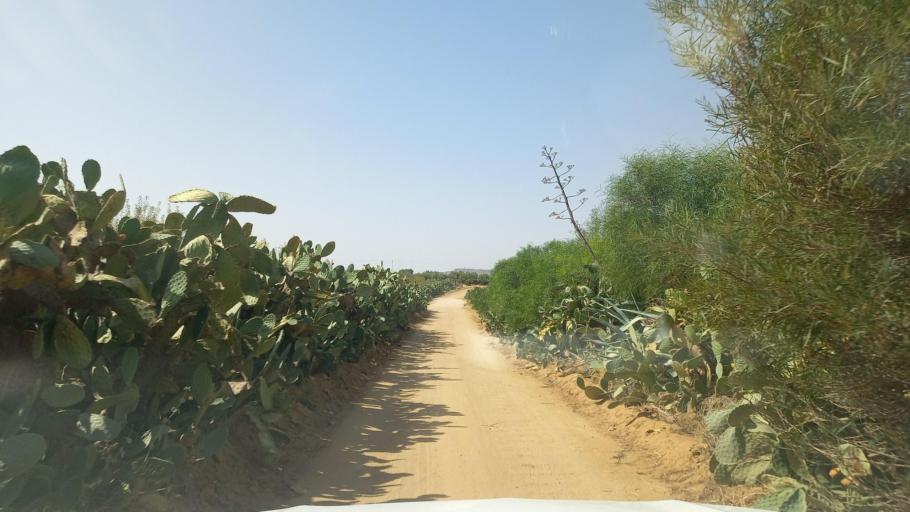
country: TN
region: Al Qasrayn
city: Kasserine
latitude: 35.2396
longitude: 9.0467
